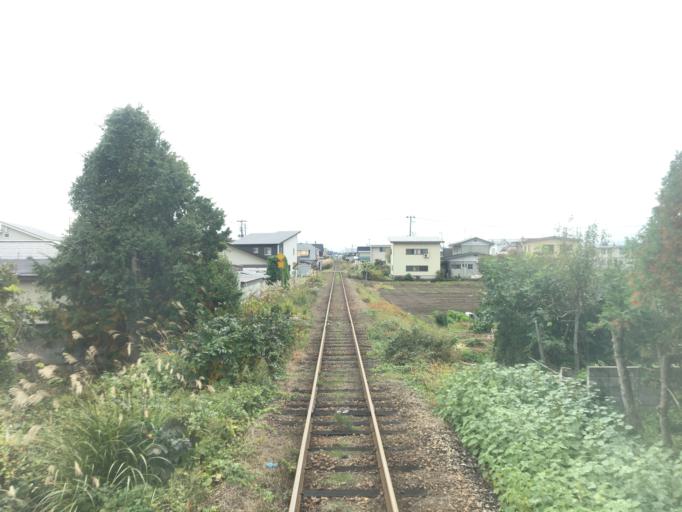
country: JP
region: Yamagata
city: Nagai
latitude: 38.1020
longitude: 140.0341
